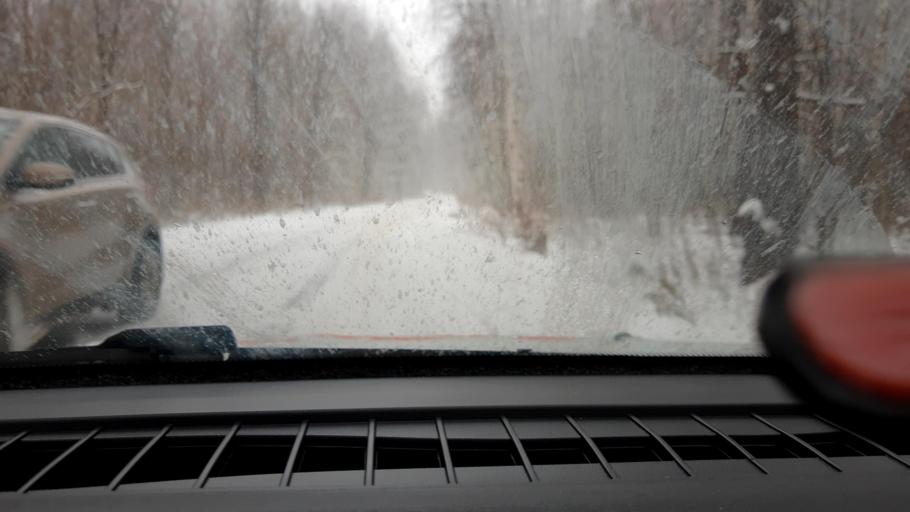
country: RU
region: Nizjnij Novgorod
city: Pamyat' Parizhskoy Kommuny
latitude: 56.0602
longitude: 44.4867
